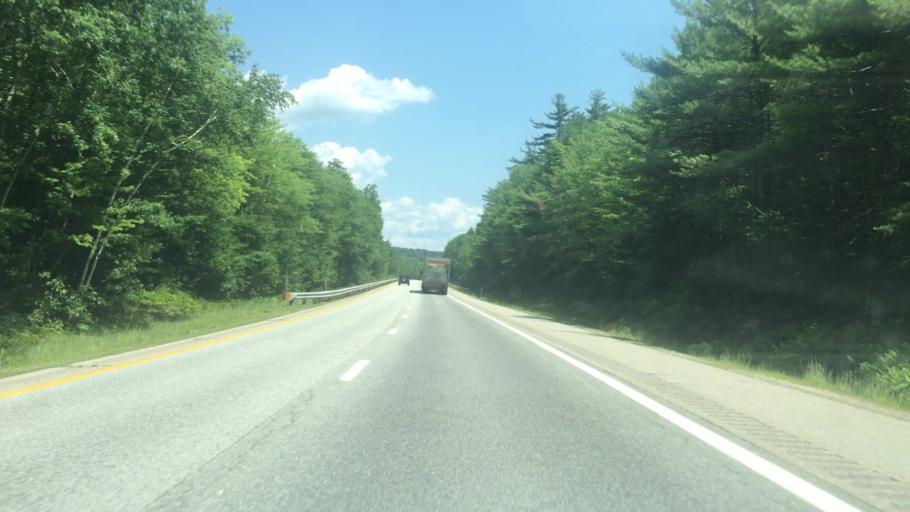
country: US
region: New Hampshire
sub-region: Merrimack County
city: Sutton
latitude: 43.3136
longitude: -71.8601
